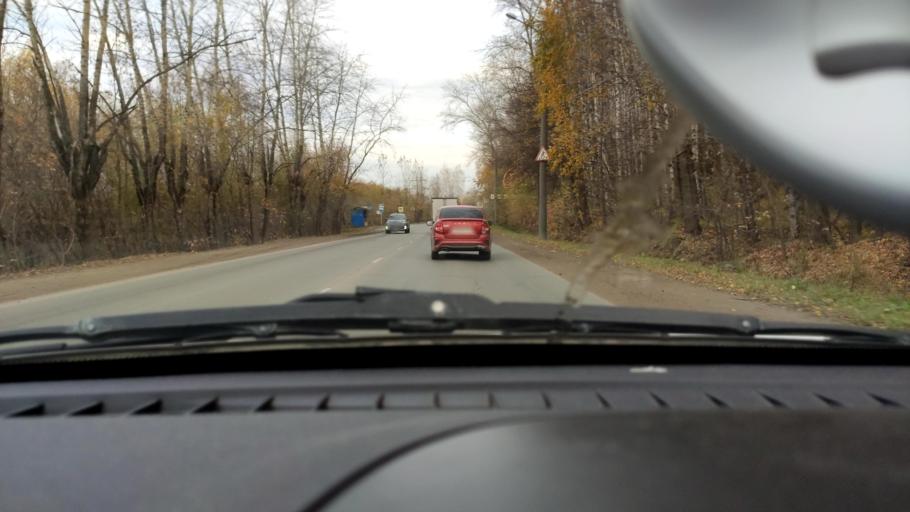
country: RU
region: Perm
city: Perm
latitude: 58.0771
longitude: 56.3497
